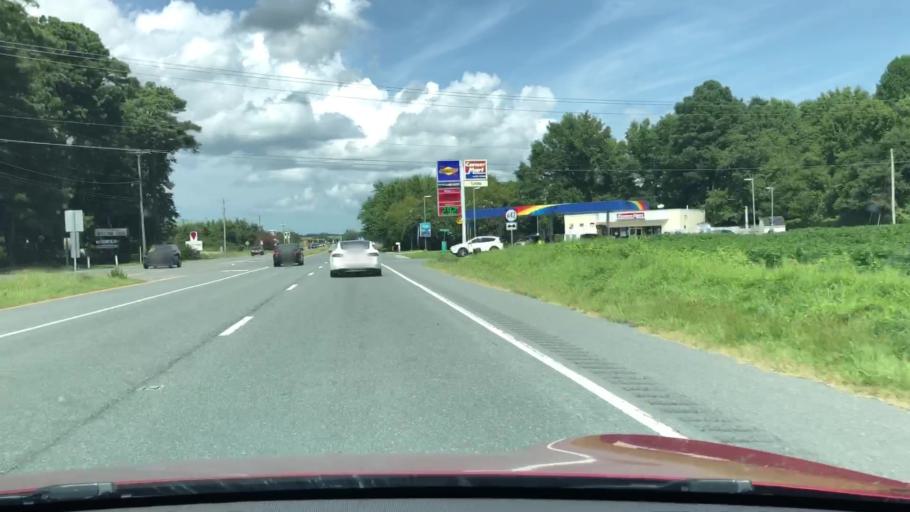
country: US
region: Virginia
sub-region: Northampton County
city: Cape Charles
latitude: 37.2654
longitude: -75.9742
